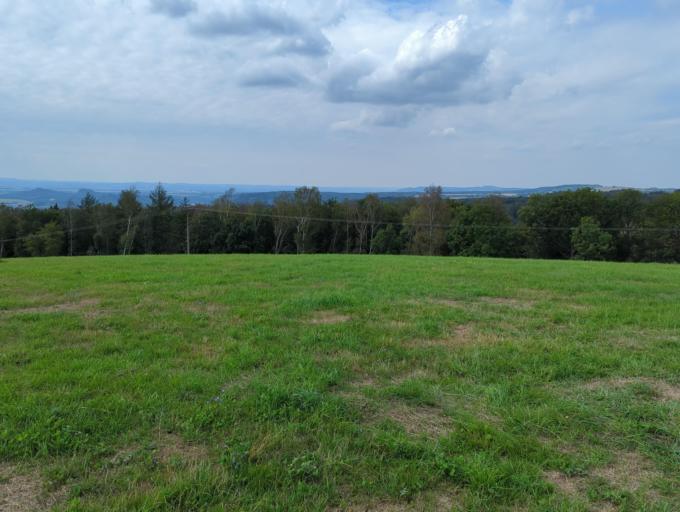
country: DE
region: Saxony
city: Porschdorf
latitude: 50.9617
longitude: 14.1423
